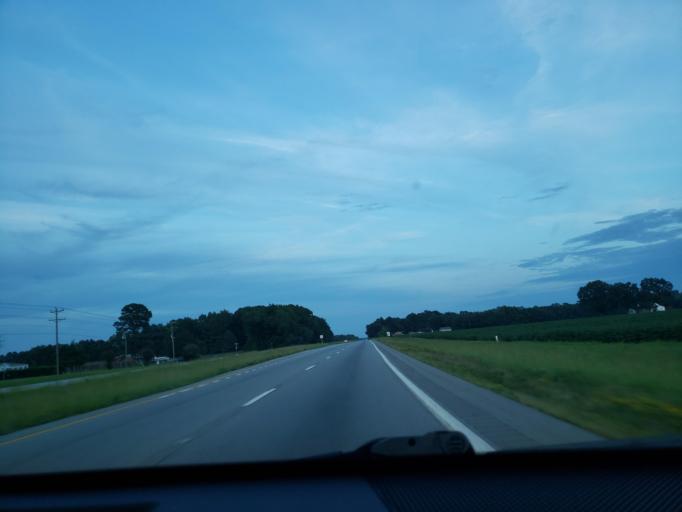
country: US
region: Virginia
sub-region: Southampton County
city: Courtland
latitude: 36.7076
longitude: -77.1365
